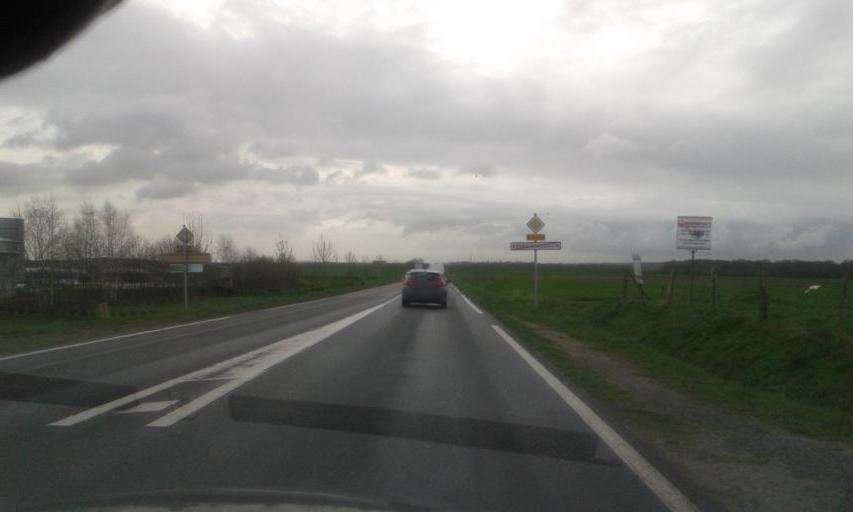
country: FR
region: Haute-Normandie
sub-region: Departement de l'Eure
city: Fleury-sur-Andelle
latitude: 49.3827
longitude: 1.3168
